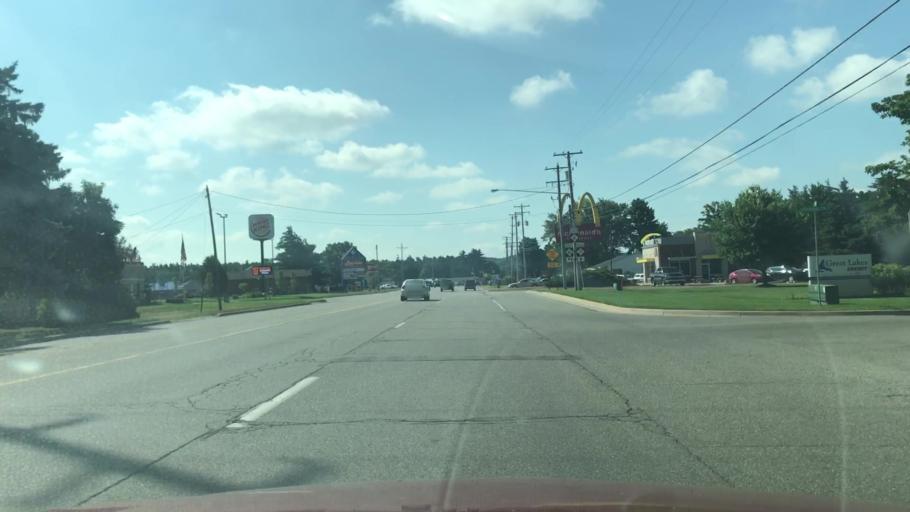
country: US
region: Michigan
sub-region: Newaygo County
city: Newaygo
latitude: 43.4073
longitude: -85.8036
